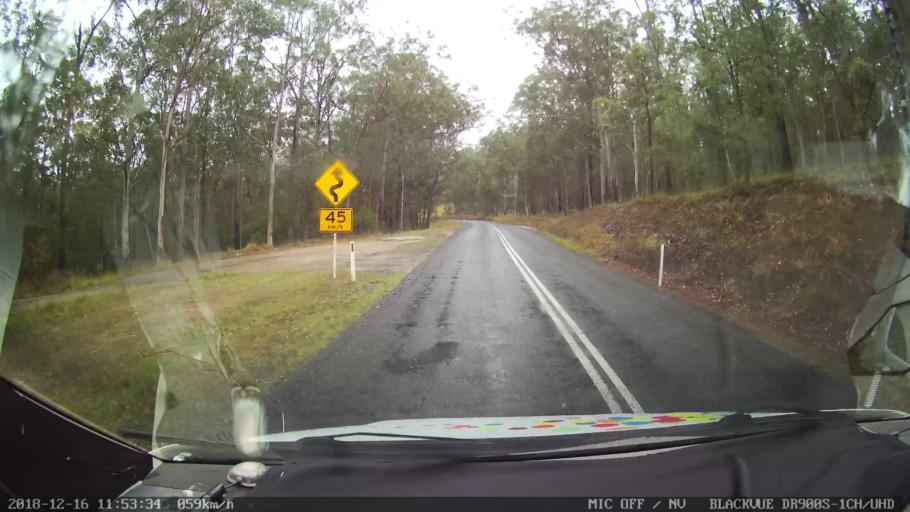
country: AU
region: New South Wales
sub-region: Tenterfield Municipality
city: Carrolls Creek
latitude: -28.9064
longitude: 152.2794
